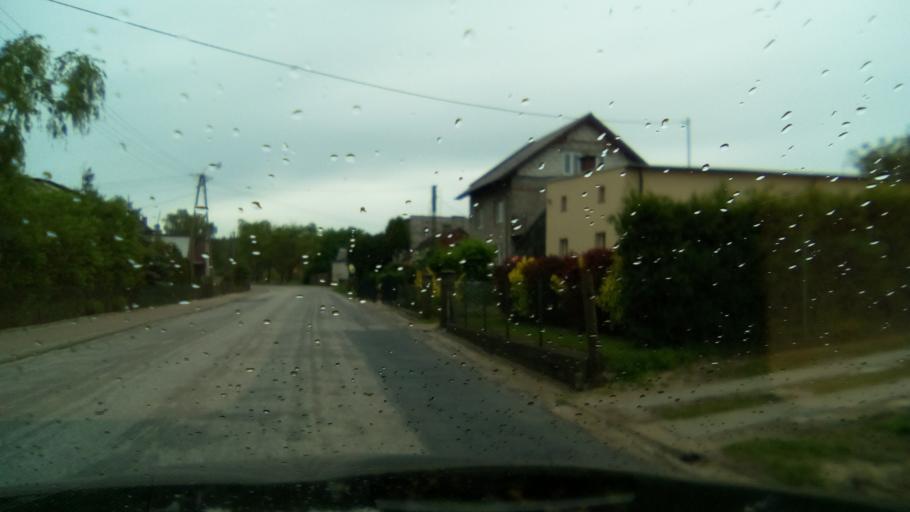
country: PL
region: Pomeranian Voivodeship
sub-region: Powiat chojnicki
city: Chojnice
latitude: 53.6273
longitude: 17.4922
